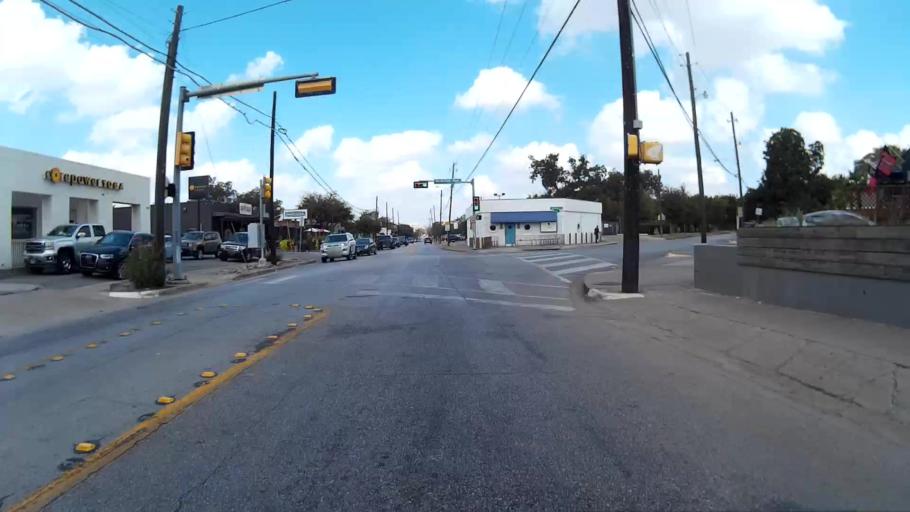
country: US
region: Texas
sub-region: Dallas County
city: Highland Park
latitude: 32.8115
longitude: -96.7746
